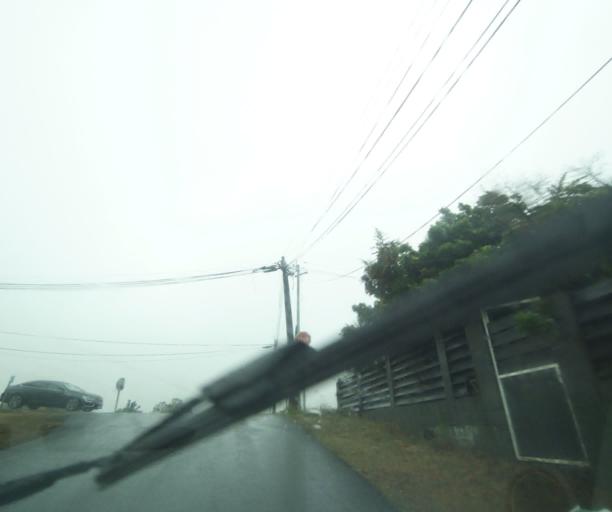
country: RE
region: Reunion
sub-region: Reunion
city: Saint-Paul
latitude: -21.0438
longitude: 55.2579
